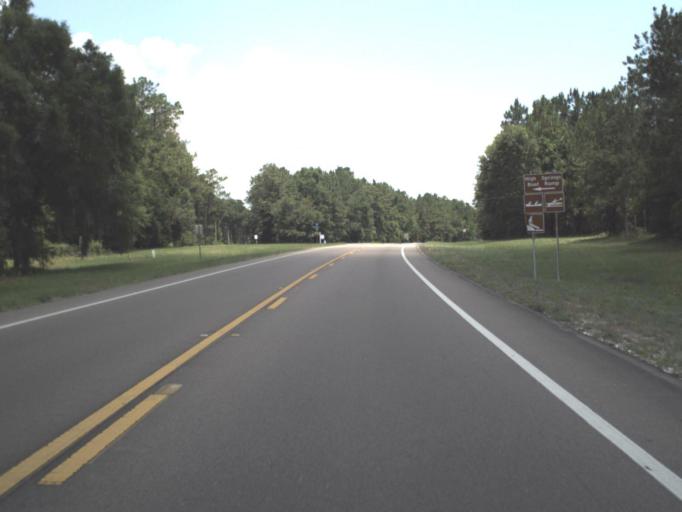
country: US
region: Florida
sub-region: Alachua County
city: High Springs
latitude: 29.8440
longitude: -82.6061
